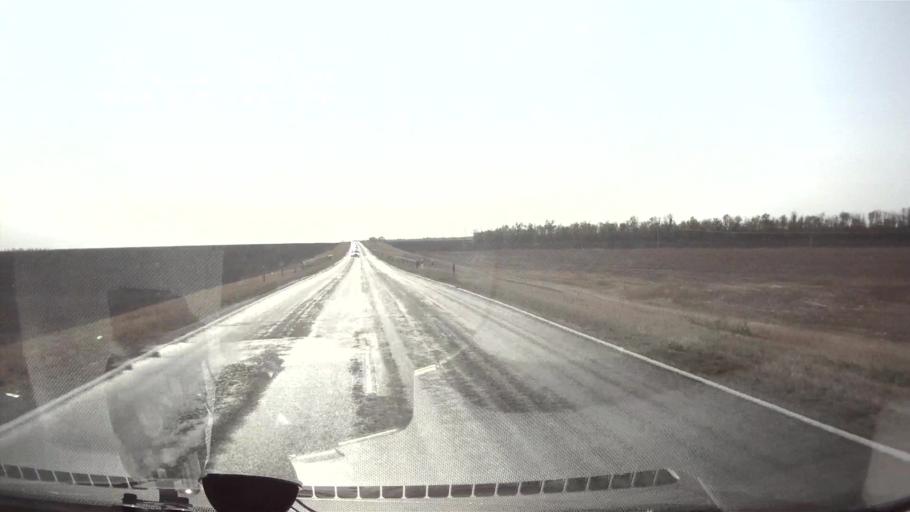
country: RU
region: Rostov
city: Peschanokopskoye
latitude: 46.3260
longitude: 40.8743
